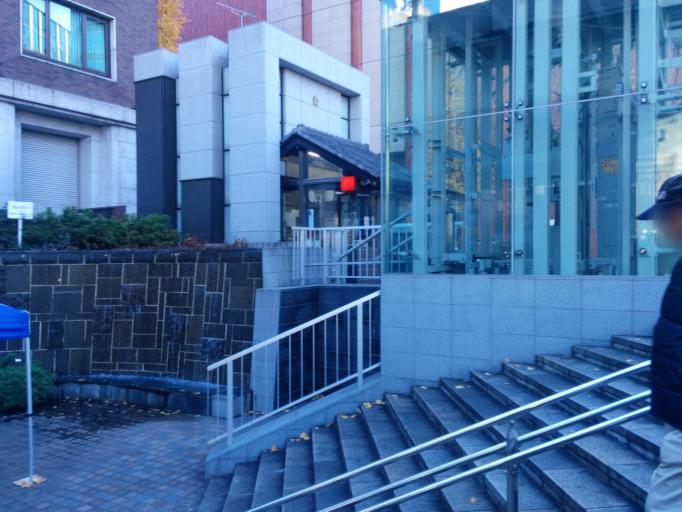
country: JP
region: Tokyo
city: Tokyo
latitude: 35.6838
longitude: 139.7746
